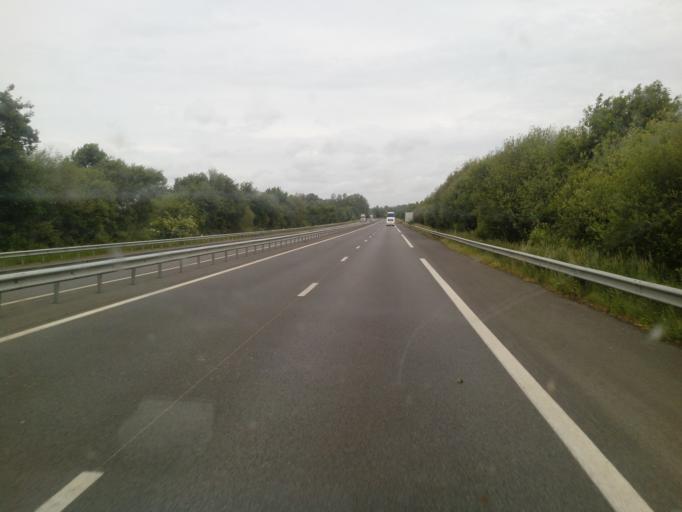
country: FR
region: Brittany
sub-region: Departement des Cotes-d'Armor
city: Broons
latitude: 48.3289
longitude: -2.2616
